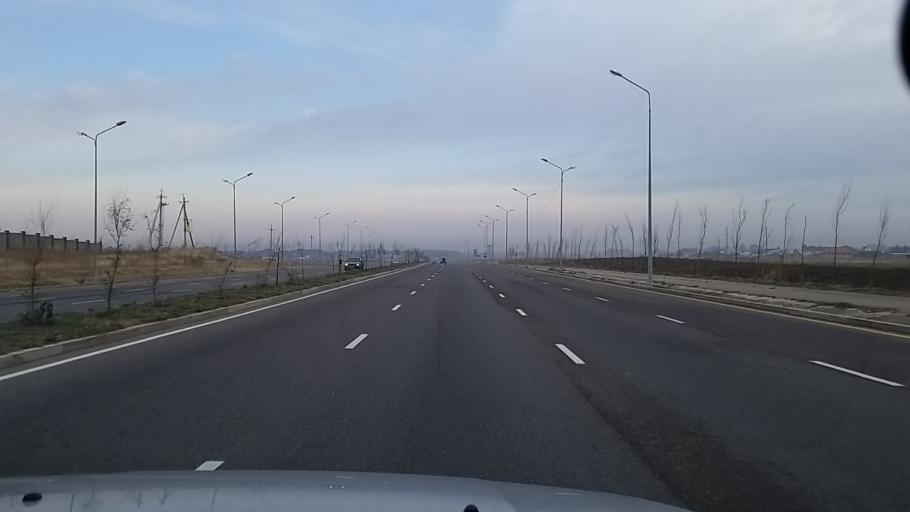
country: KZ
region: Almaty Oblysy
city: Burunday
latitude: 43.3400
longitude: 76.8337
